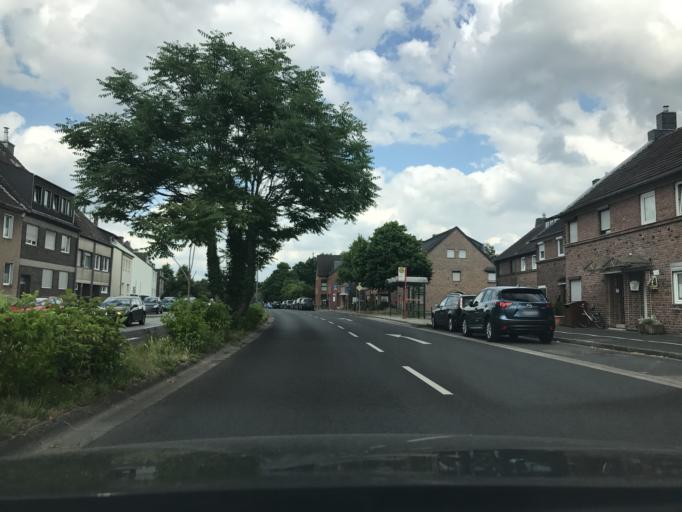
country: DE
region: North Rhine-Westphalia
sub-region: Regierungsbezirk Dusseldorf
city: Neuss
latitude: 51.2217
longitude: 6.6731
